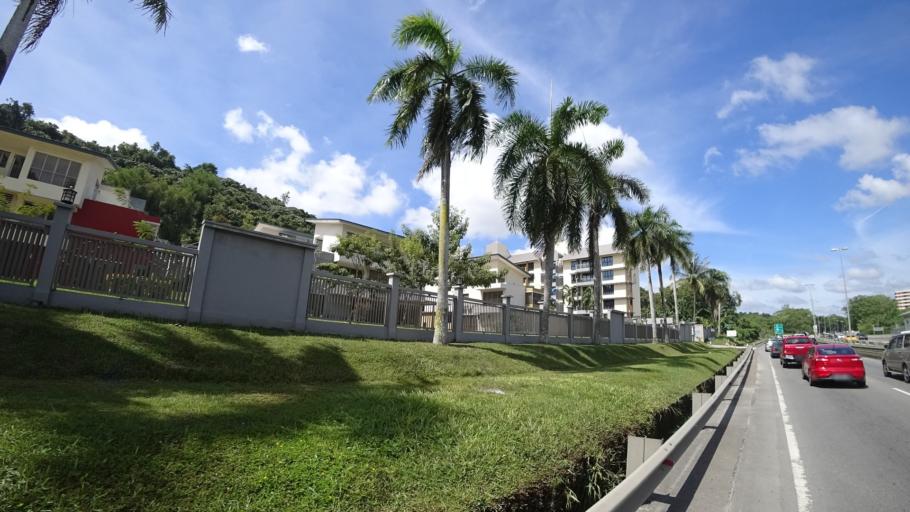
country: BN
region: Brunei and Muara
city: Bandar Seri Begawan
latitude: 4.8611
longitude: 114.8975
